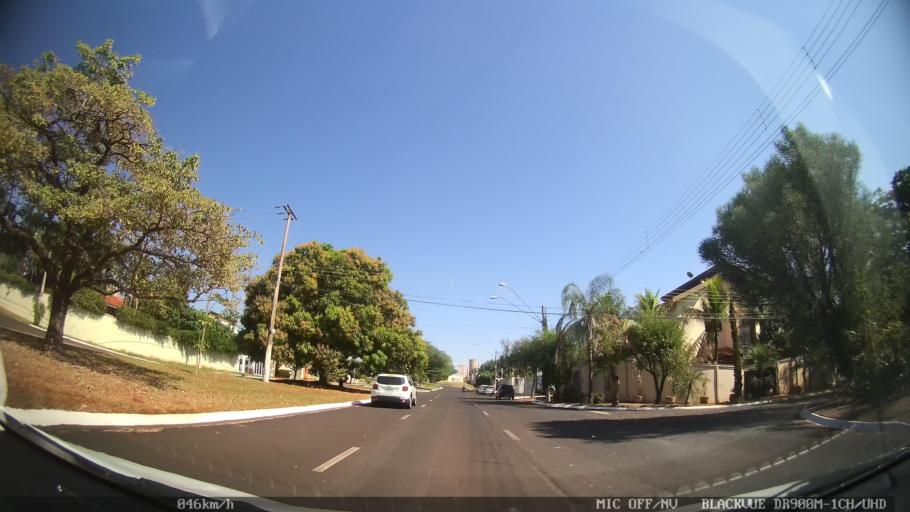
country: BR
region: Sao Paulo
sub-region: Ribeirao Preto
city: Ribeirao Preto
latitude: -21.2161
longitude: -47.7868
